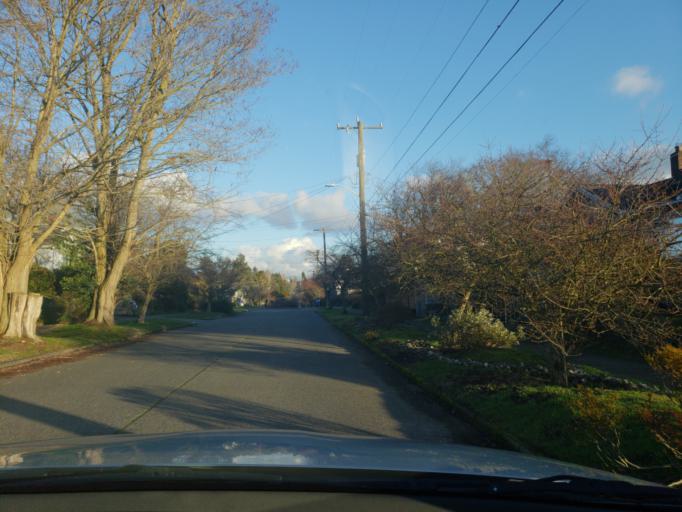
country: US
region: Washington
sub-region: King County
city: Shoreline
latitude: 47.6833
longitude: -122.3693
